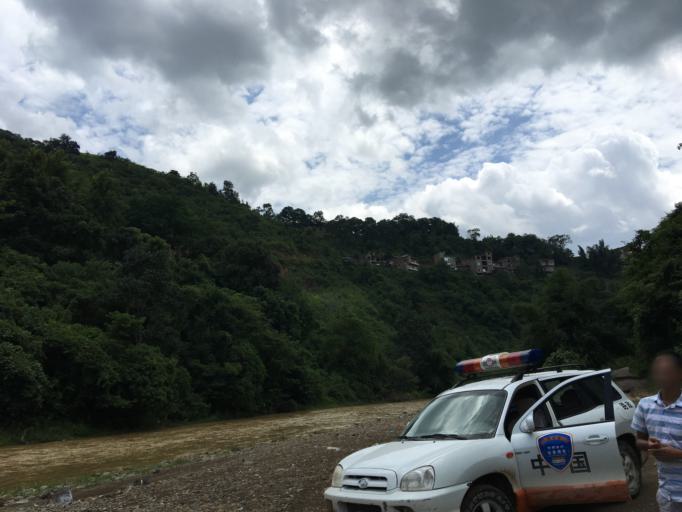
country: CN
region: Guangxi Zhuangzu Zizhiqu
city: Xinzhou
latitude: 25.0491
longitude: 105.8935
